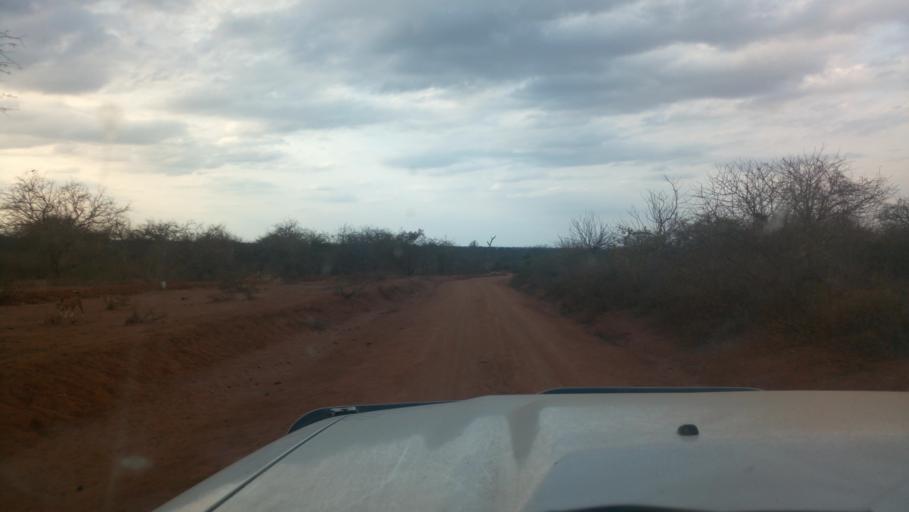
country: KE
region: Makueni
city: Wote
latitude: -1.9103
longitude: 38.0454
